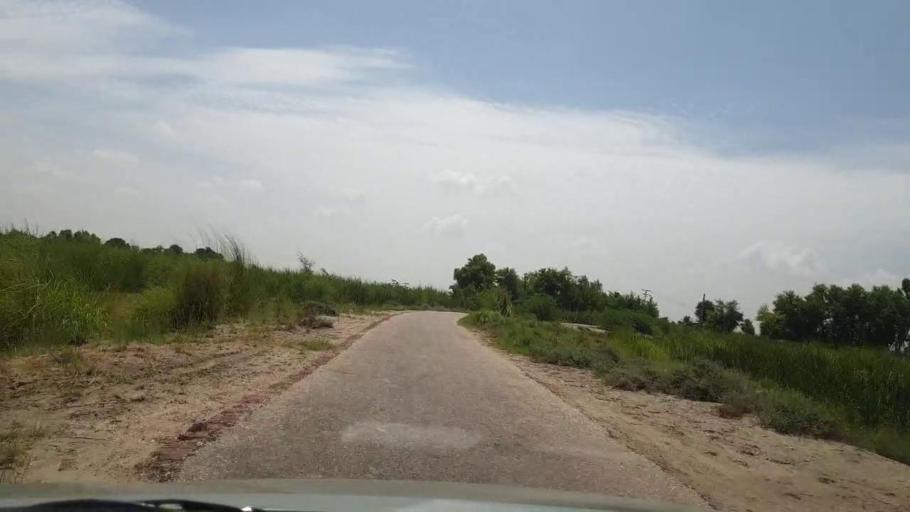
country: PK
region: Sindh
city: Bozdar
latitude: 27.0672
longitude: 68.9817
